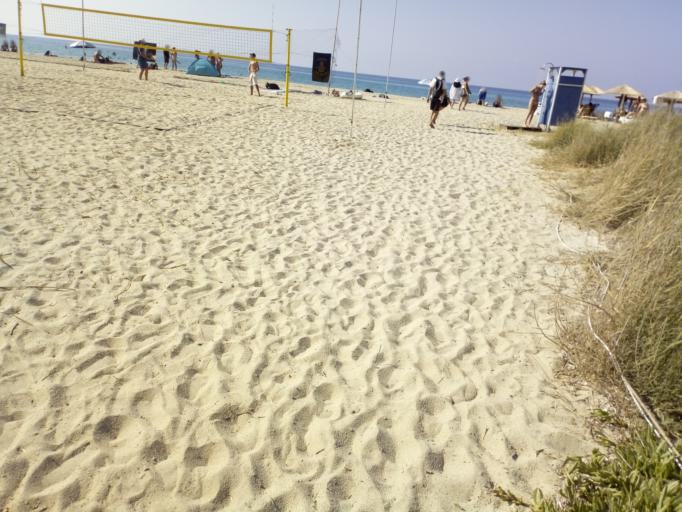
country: GR
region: North Aegean
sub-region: Nomos Samou
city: Agios Kirykos
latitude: 37.6302
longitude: 26.0987
